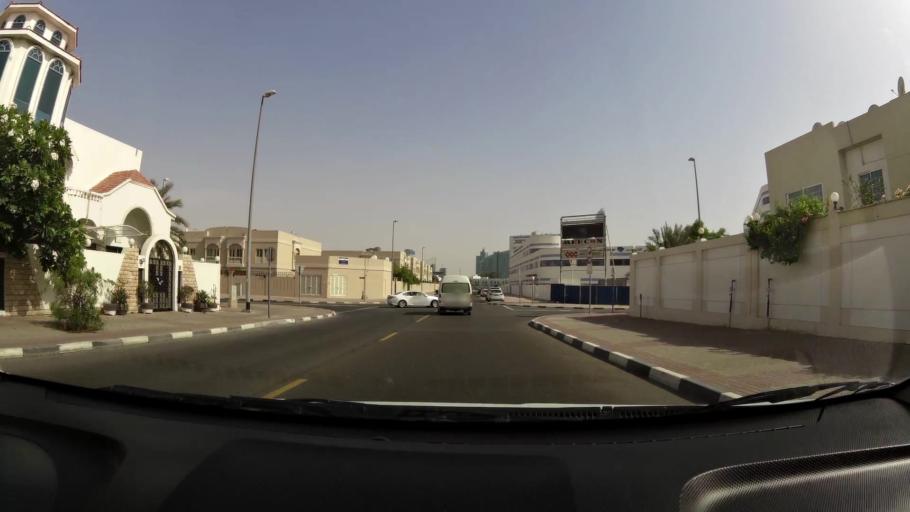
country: AE
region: Ash Shariqah
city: Sharjah
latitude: 25.2409
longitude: 55.3476
